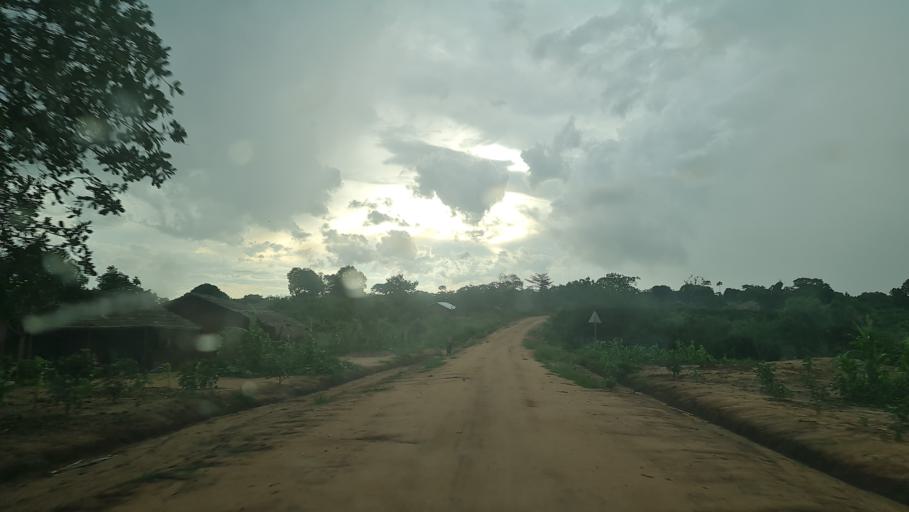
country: MZ
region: Nampula
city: Nacala
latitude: -14.0047
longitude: 40.3553
